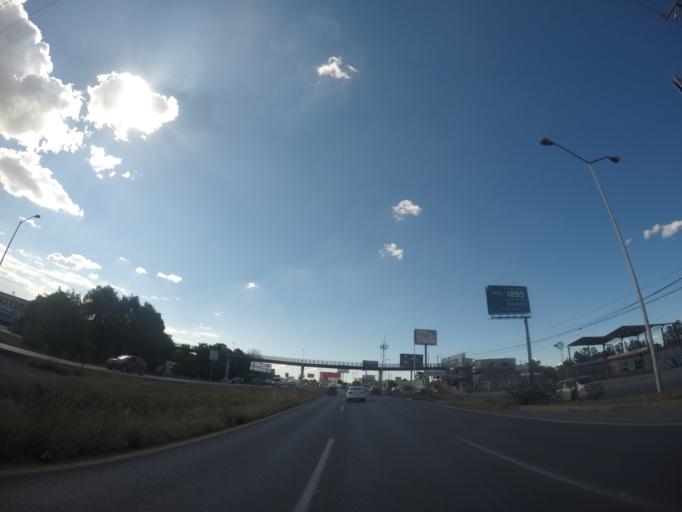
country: MX
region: San Luis Potosi
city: La Pila
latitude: 22.1067
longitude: -100.8909
